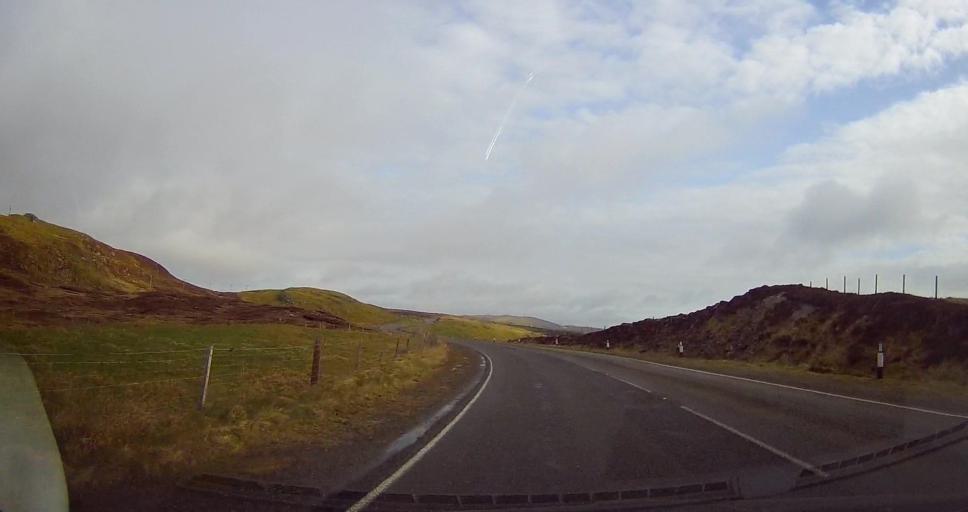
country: GB
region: Scotland
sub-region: Shetland Islands
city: Lerwick
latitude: 60.1057
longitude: -1.2192
